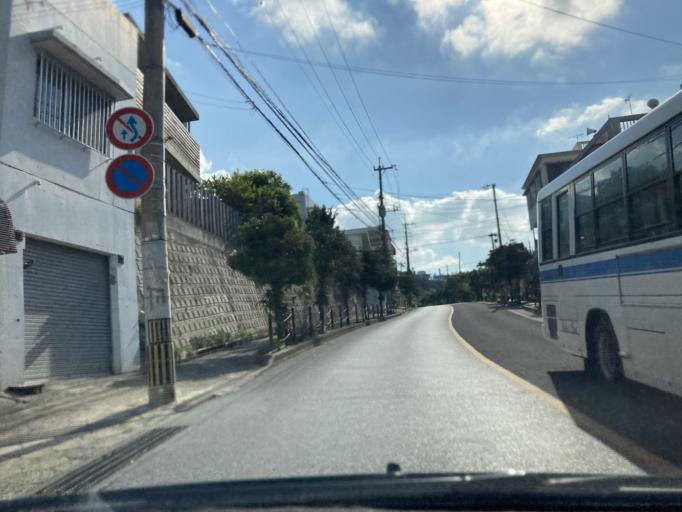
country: JP
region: Okinawa
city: Naha-shi
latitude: 26.2138
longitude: 127.7162
